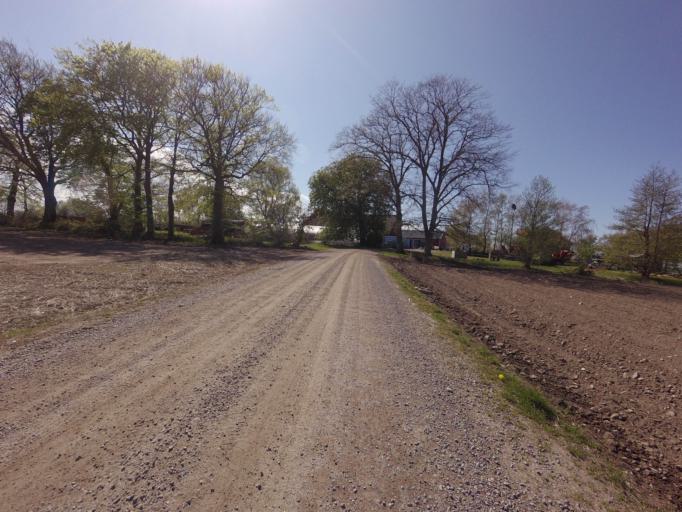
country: SE
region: Skane
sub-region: Helsingborg
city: Odakra
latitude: 56.1297
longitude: 12.6451
